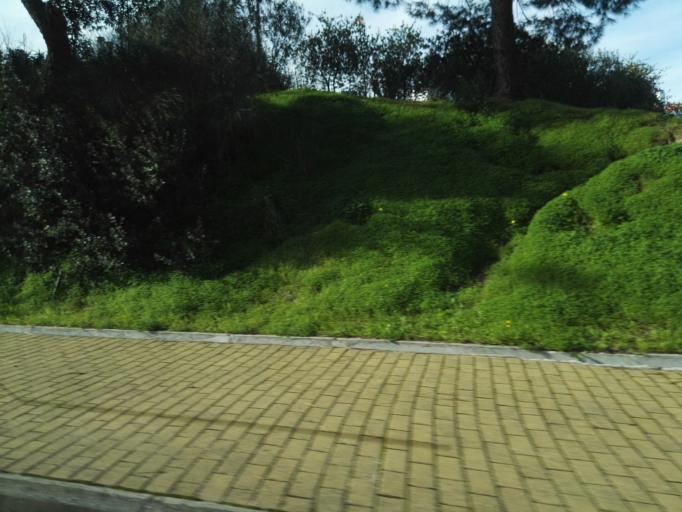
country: PT
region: Evora
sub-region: Mora
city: Mora
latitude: 38.9409
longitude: -8.1646
